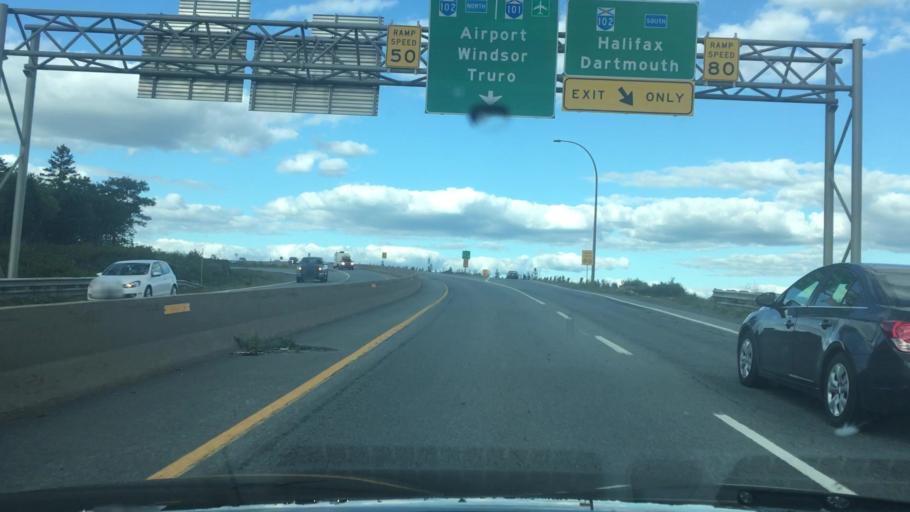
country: CA
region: Nova Scotia
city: Halifax
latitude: 44.6422
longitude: -63.6556
